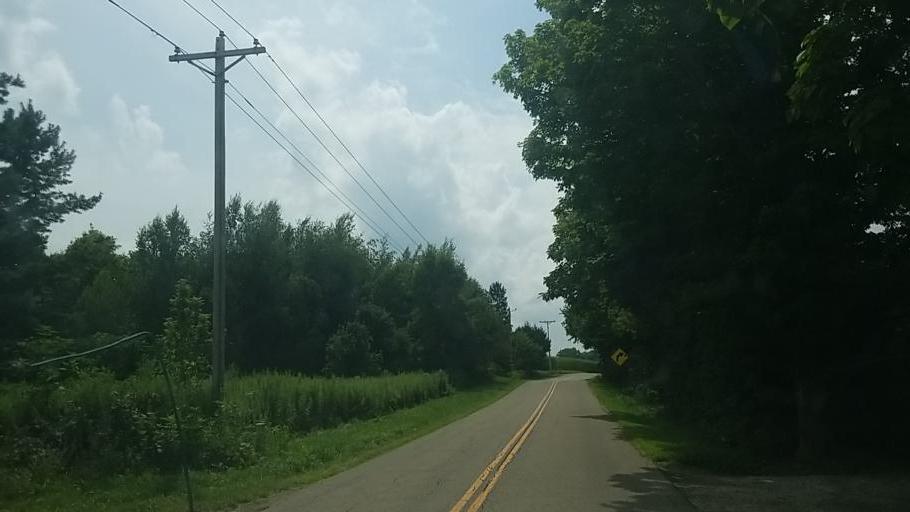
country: US
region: Ohio
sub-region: Knox County
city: Gambier
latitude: 40.3210
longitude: -82.4399
